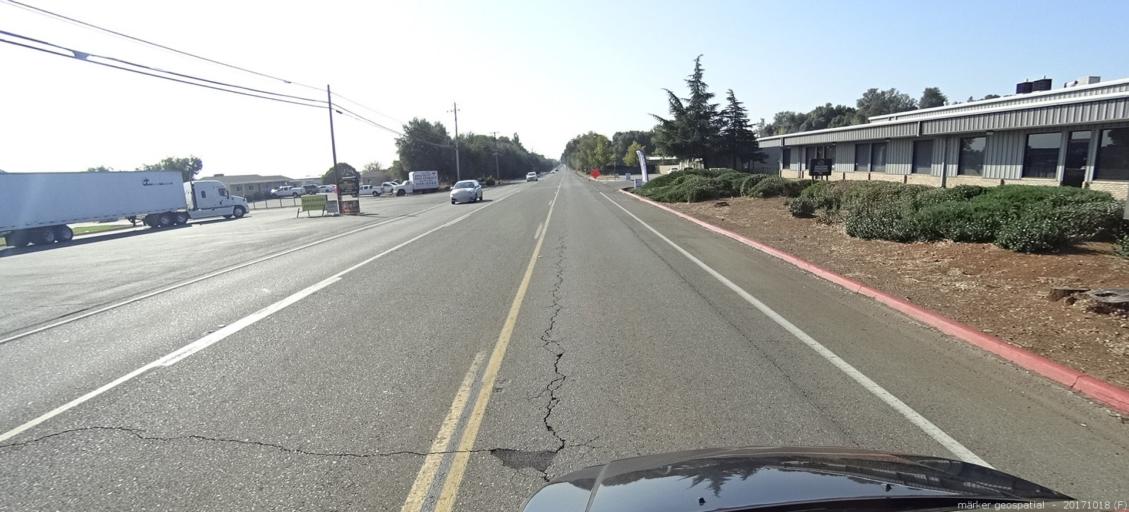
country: US
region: California
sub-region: Shasta County
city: Palo Cedro
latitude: 40.5451
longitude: -122.3028
